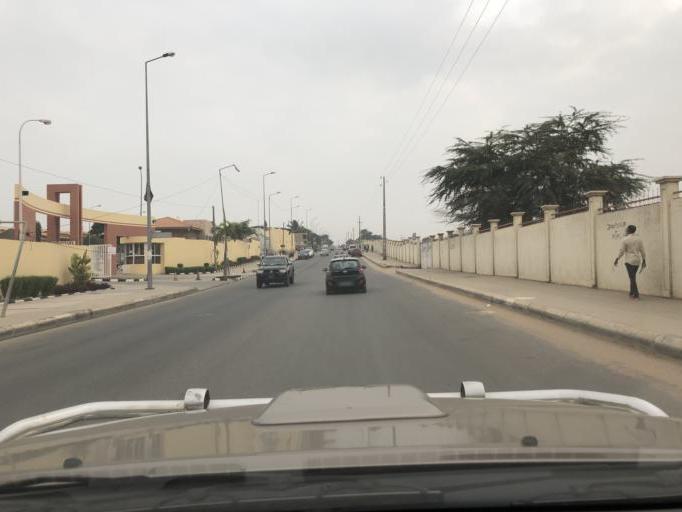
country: AO
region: Luanda
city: Luanda
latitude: -8.9036
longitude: 13.2156
